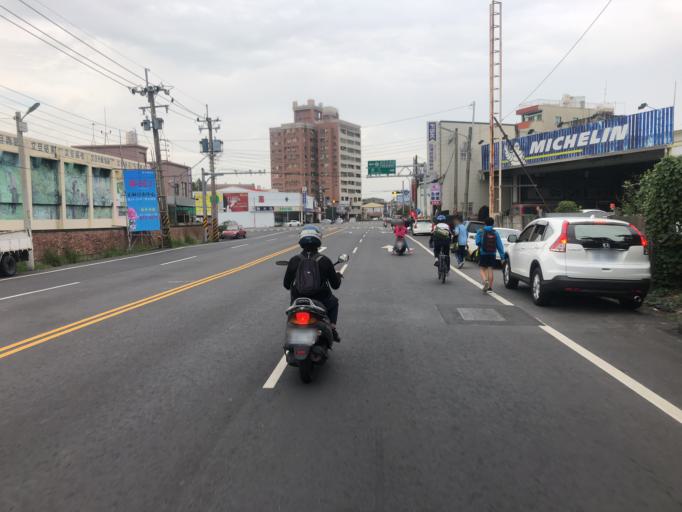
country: TW
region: Taiwan
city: Xinying
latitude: 23.1754
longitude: 120.2470
